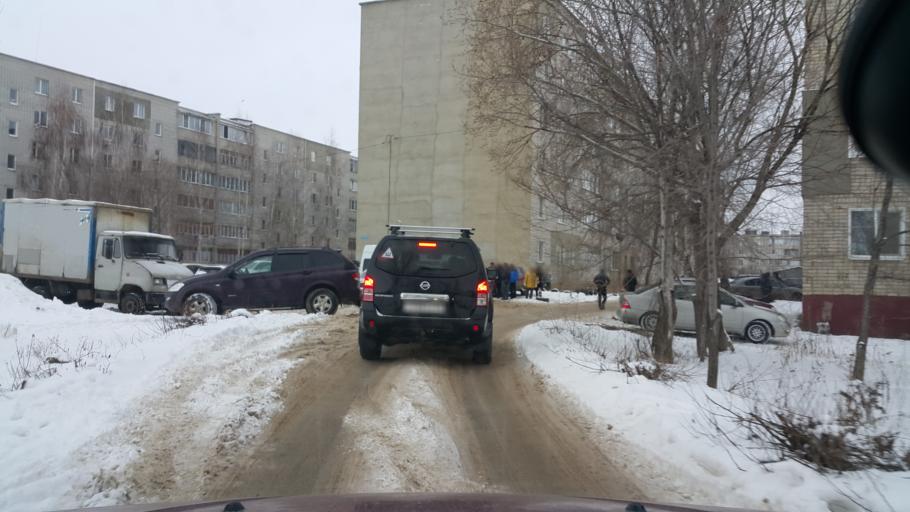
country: RU
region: Tambov
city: Bokino
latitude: 52.6386
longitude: 41.4421
